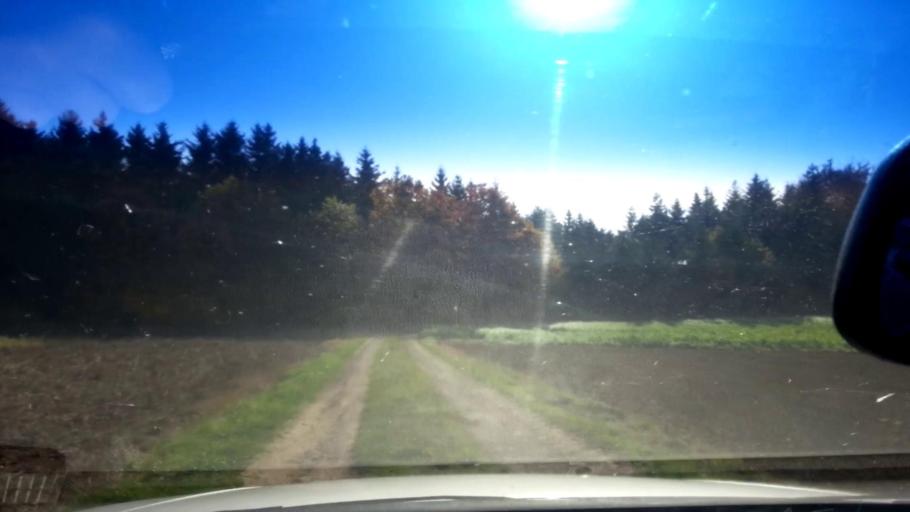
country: DE
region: Bavaria
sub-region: Upper Franconia
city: Wonsees
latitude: 49.9643
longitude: 11.2690
